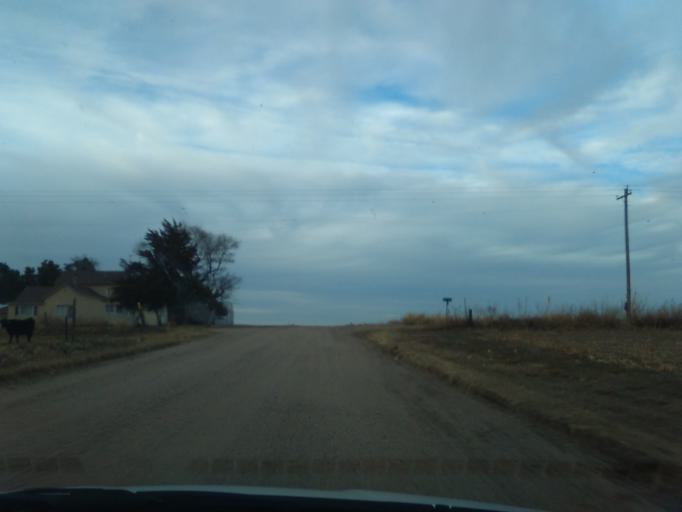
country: US
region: Nebraska
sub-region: Furnas County
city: Cambridge
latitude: 40.3215
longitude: -100.0435
